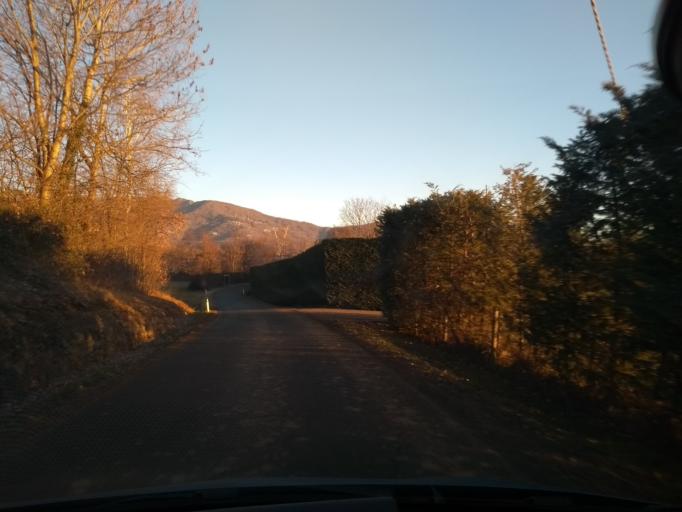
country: IT
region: Piedmont
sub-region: Provincia di Torino
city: Mathi
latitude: 45.2834
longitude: 7.5450
